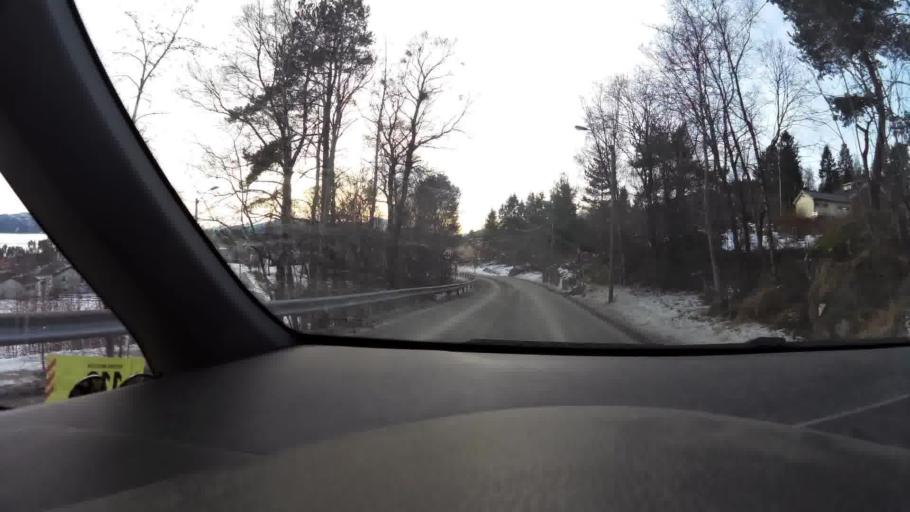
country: NO
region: More og Romsdal
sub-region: Kristiansund
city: Rensvik
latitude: 63.0683
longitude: 7.8734
